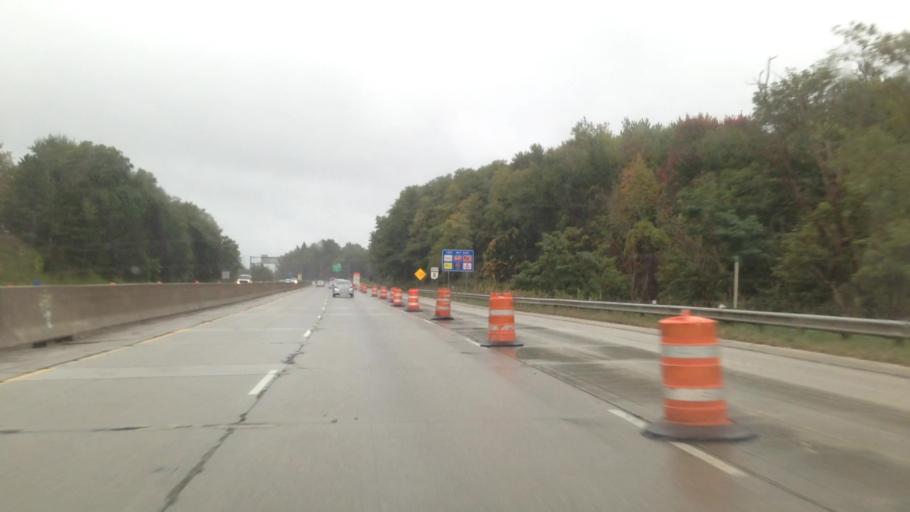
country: US
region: Ohio
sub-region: Summit County
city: Silver Lake
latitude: 41.1752
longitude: -81.4795
